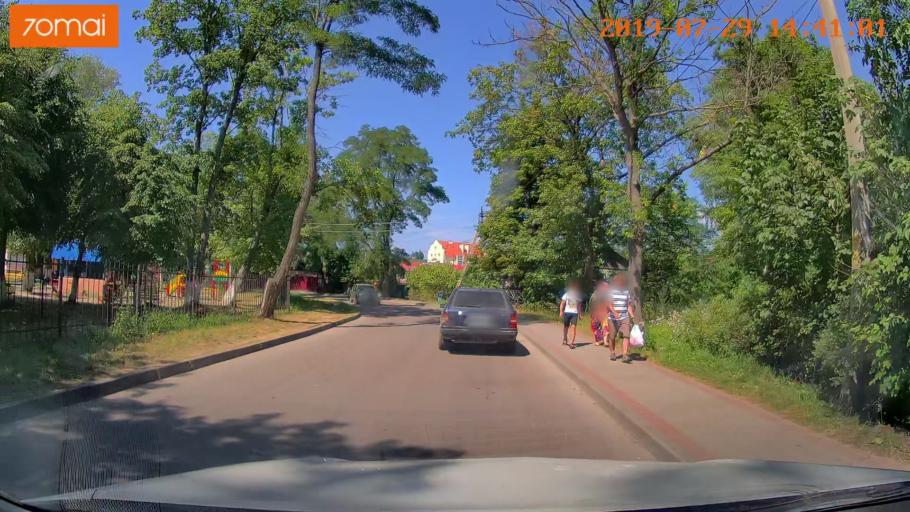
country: RU
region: Kaliningrad
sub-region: Gorod Kaliningrad
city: Baltiysk
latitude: 54.6565
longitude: 19.9004
